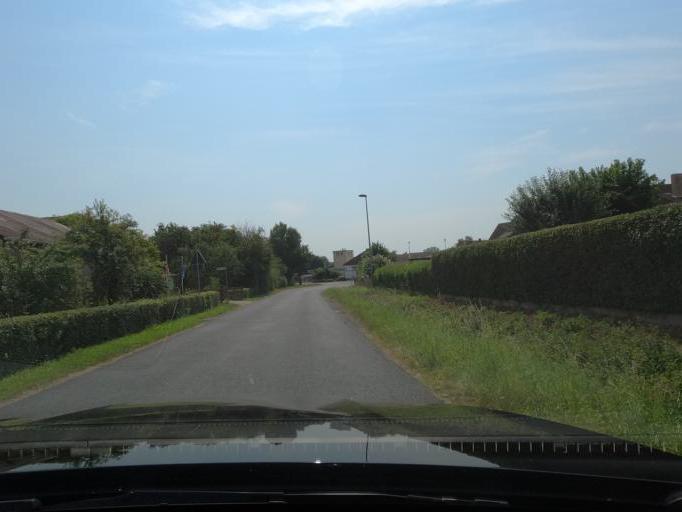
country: DE
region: Lower Saxony
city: Elze
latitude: 52.1765
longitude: 9.7267
